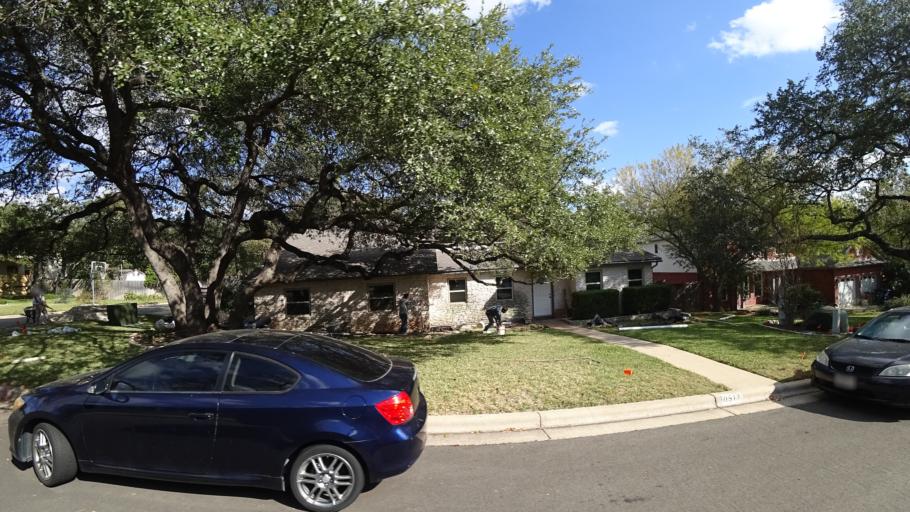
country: US
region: Texas
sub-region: Williamson County
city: Jollyville
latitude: 30.4260
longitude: -97.7955
